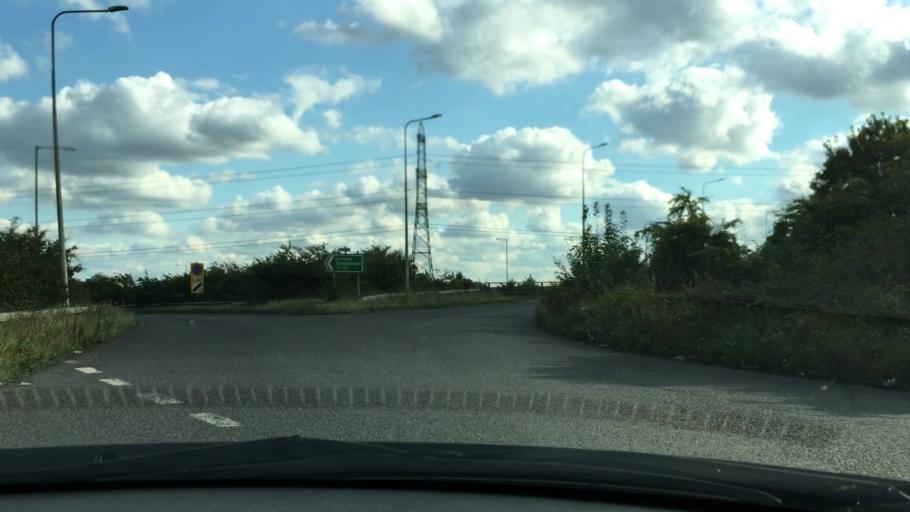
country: GB
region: England
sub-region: North East Lincolnshire
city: Immingham
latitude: 53.5982
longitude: -0.1966
